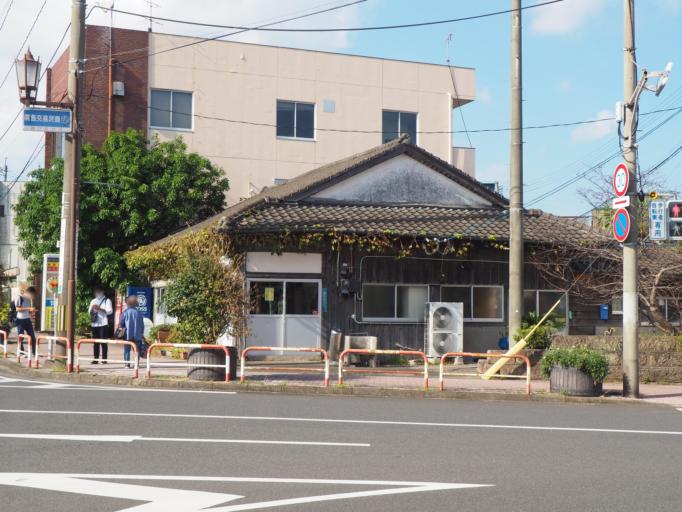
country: JP
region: Kagoshima
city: Ibusuki
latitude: 31.2373
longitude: 130.6431
